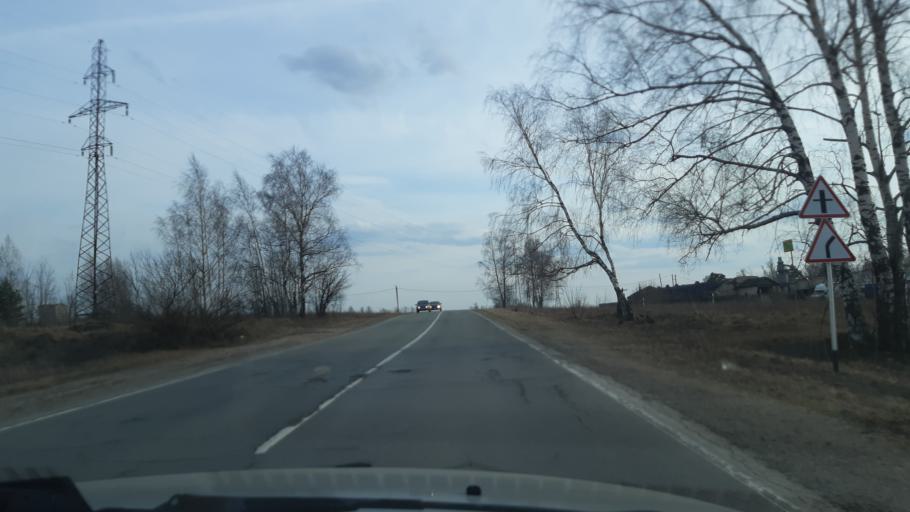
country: RU
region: Vladimir
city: Luknovo
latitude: 56.2017
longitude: 42.0334
